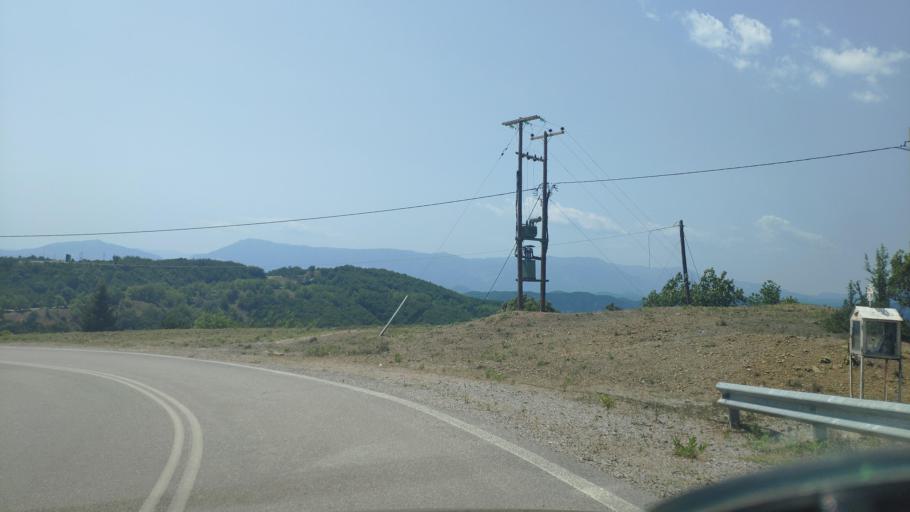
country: GR
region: Epirus
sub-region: Nomos Artas
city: Ano Kalentini
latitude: 39.2408
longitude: 21.2054
